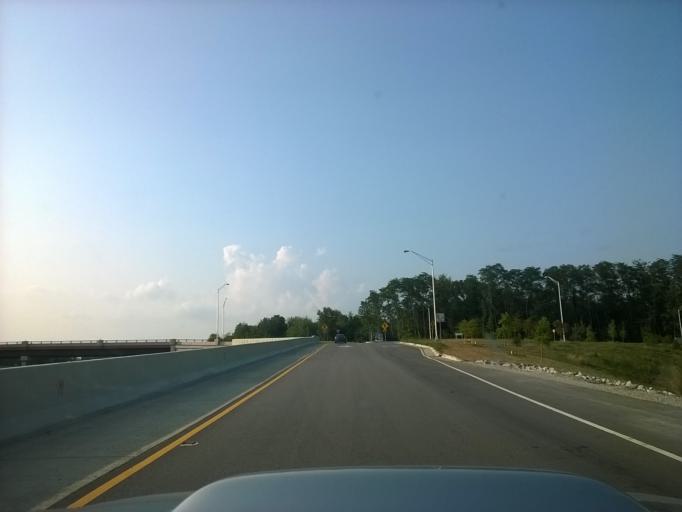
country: US
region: Indiana
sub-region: Hamilton County
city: Westfield
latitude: 40.0207
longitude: -86.1309
